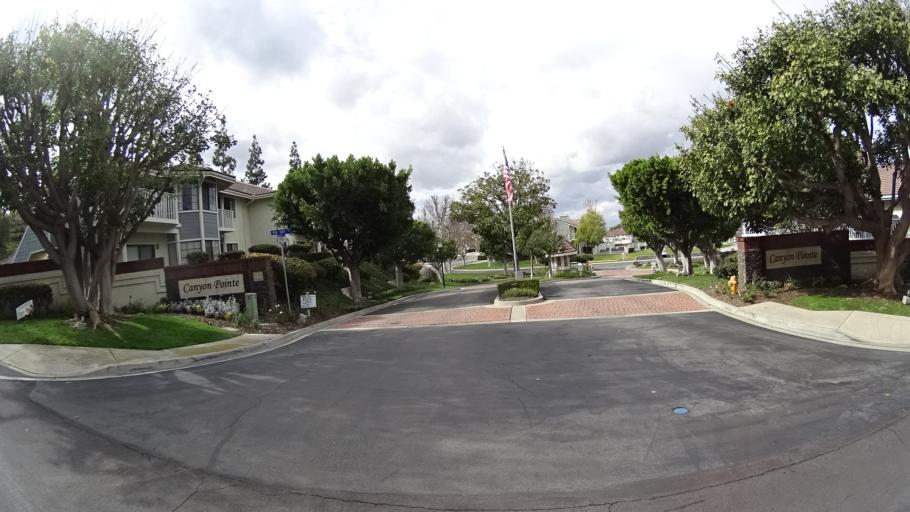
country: US
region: California
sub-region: Orange County
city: Villa Park
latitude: 33.8391
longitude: -117.7923
